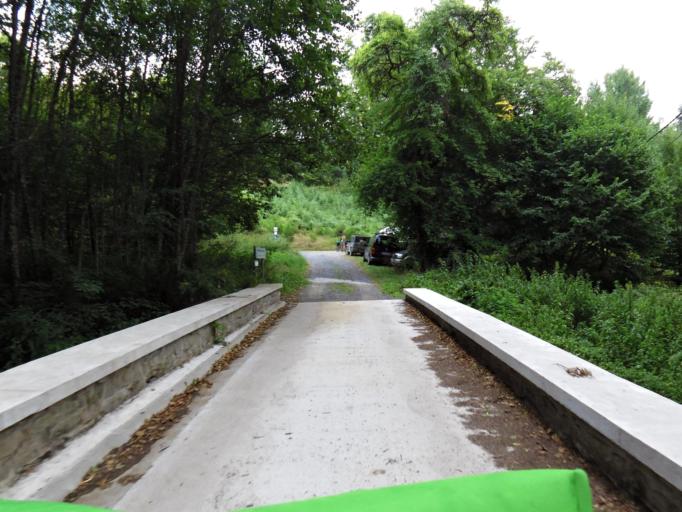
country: BE
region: Wallonia
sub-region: Province de Namur
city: Bievre
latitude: 49.8691
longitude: 4.9933
